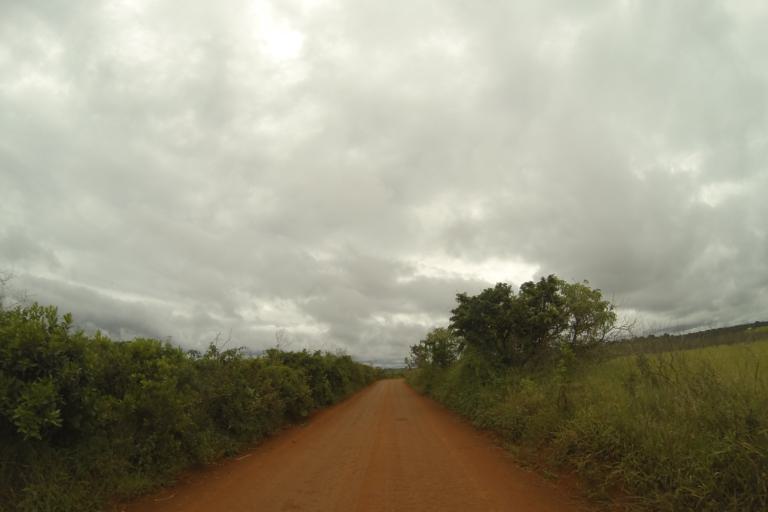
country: BR
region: Minas Gerais
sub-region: Campos Altos
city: Campos Altos
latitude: -19.8780
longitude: -46.3010
